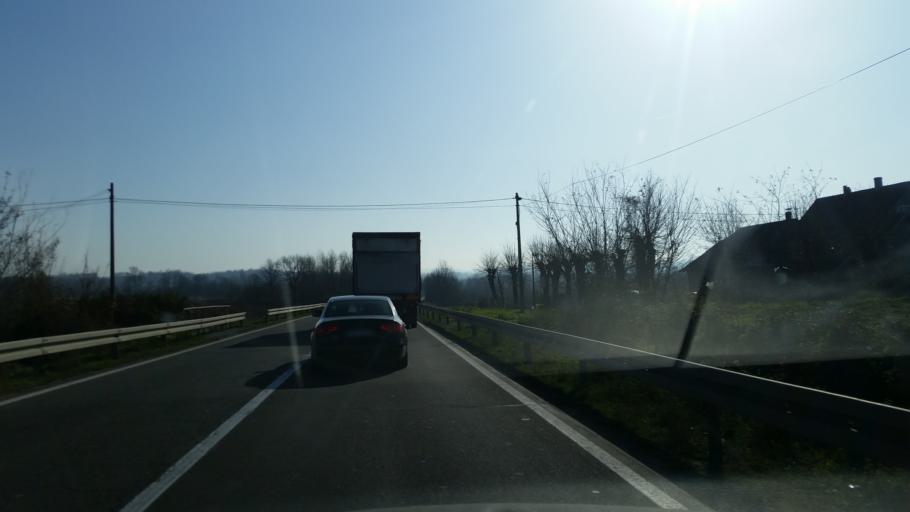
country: RS
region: Central Serbia
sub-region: Kolubarski Okrug
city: Ljig
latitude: 44.2833
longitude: 20.2757
